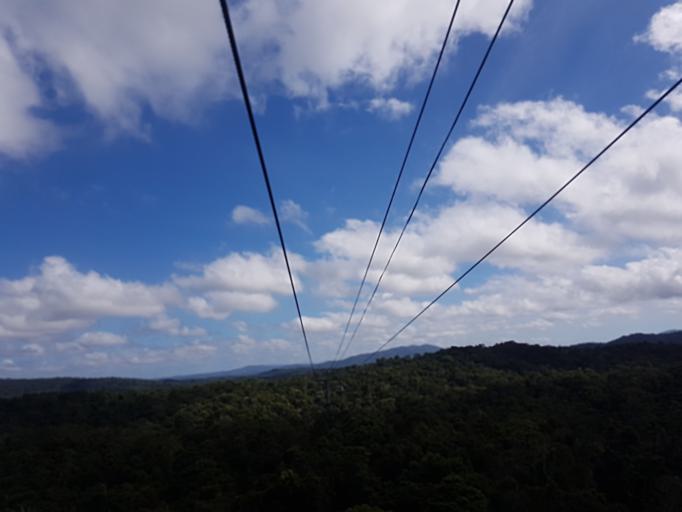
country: AU
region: Queensland
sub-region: Tablelands
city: Kuranda
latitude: -16.8439
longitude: 145.6613
